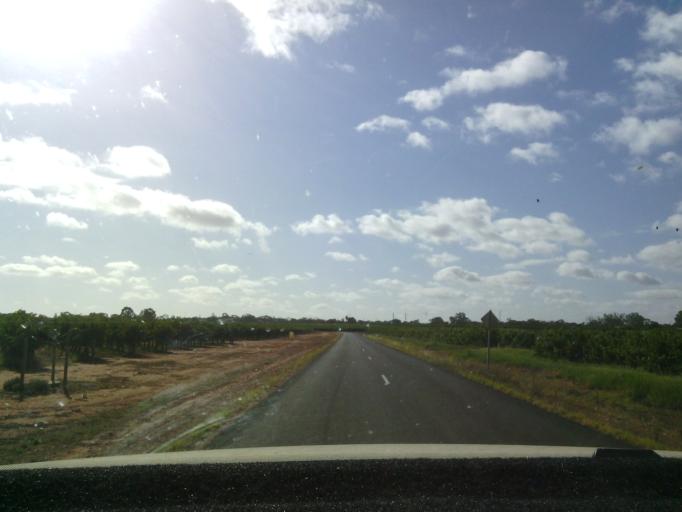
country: AU
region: South Australia
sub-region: Berri and Barmera
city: Monash
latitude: -34.2338
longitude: 140.5613
